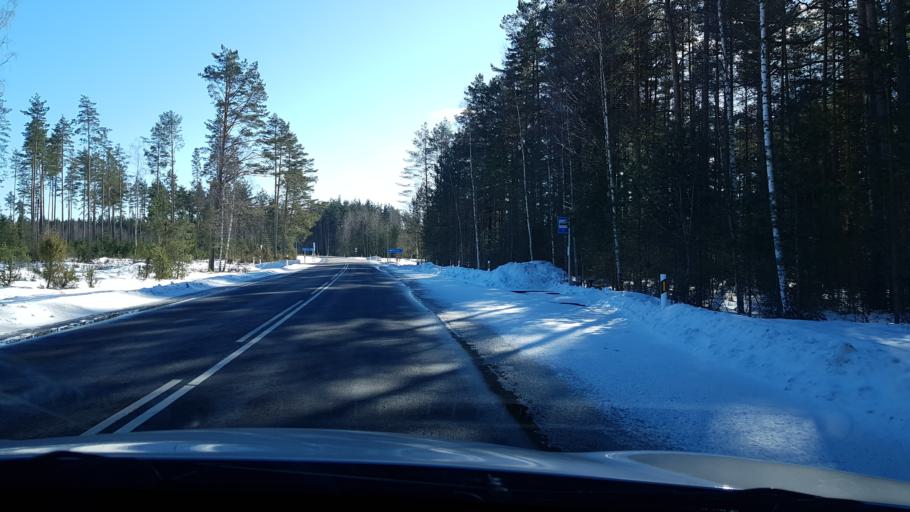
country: EE
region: Polvamaa
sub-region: Raepina vald
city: Rapina
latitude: 57.9840
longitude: 27.5662
